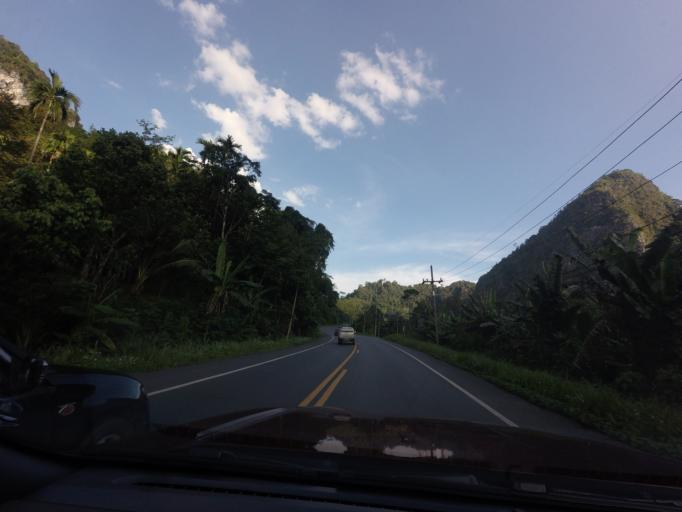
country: TH
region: Yala
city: Than To
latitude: 6.2126
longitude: 101.1666
